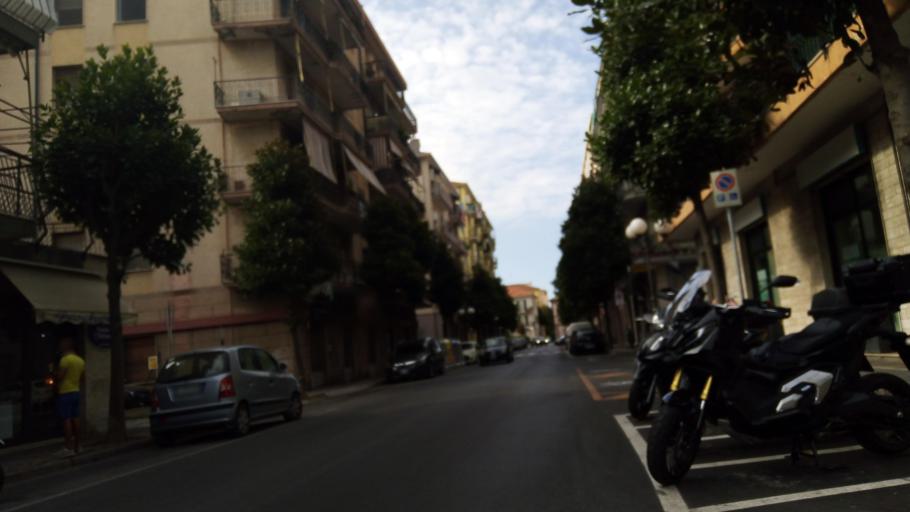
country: IT
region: Liguria
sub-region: Provincia di Savona
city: Albenga
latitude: 44.0493
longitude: 8.2207
